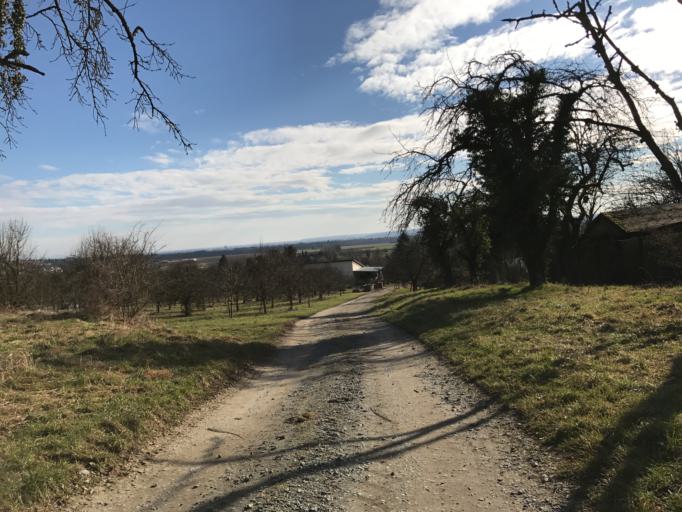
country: DE
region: Hesse
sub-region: Regierungsbezirk Darmstadt
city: Niedernhausen
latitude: 50.0978
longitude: 8.3094
